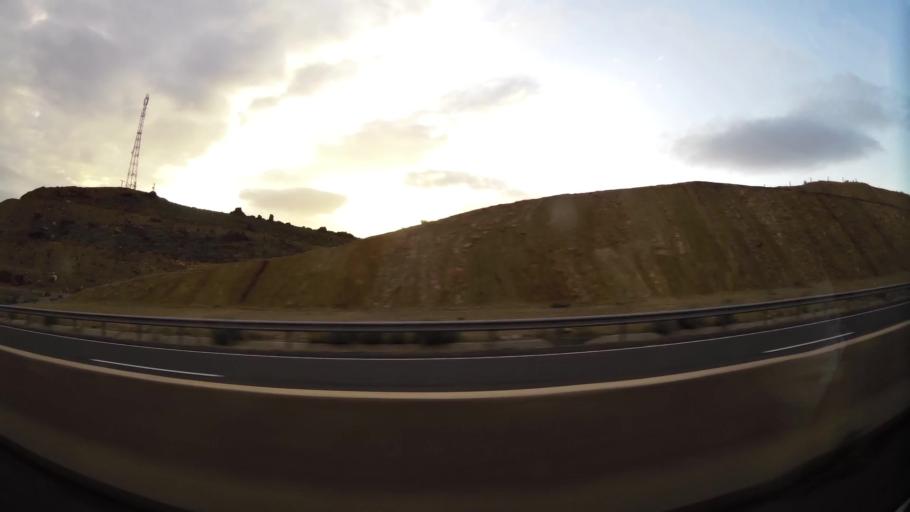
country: MA
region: Oriental
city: Taourirt
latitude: 34.4921
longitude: -2.9700
